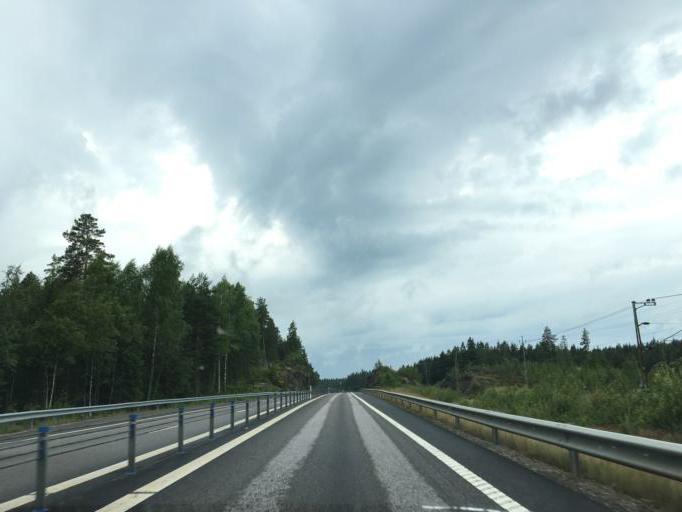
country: SE
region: OEstergoetland
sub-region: Norrkopings Kommun
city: Jursla
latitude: 58.8266
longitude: 16.1832
